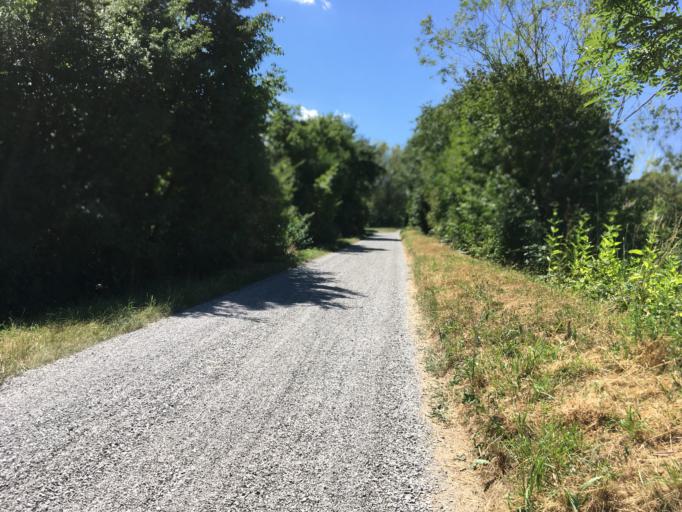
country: DE
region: Baden-Wuerttemberg
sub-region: Karlsruhe Region
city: Muhlacker
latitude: 48.9316
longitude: 8.8706
